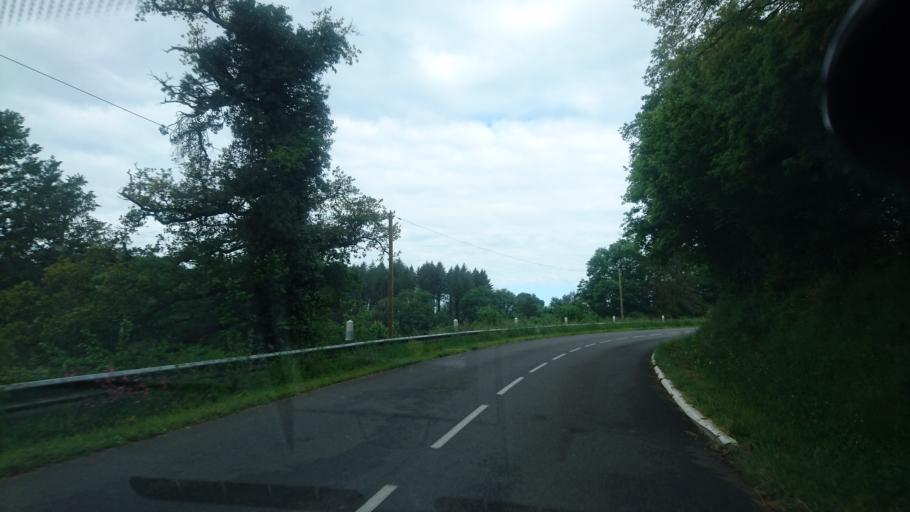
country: FR
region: Limousin
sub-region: Departement de la Haute-Vienne
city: Saint-Germain-les-Belles
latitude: 45.6049
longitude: 1.4826
